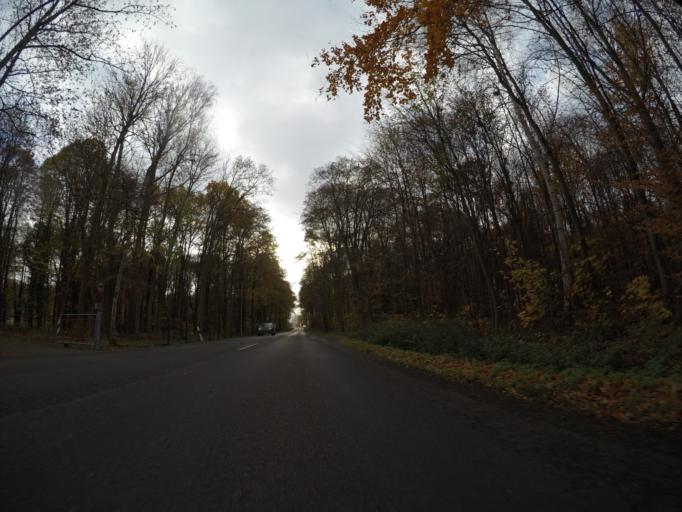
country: DE
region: Thuringia
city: Altenburg
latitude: 50.9714
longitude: 12.4329
